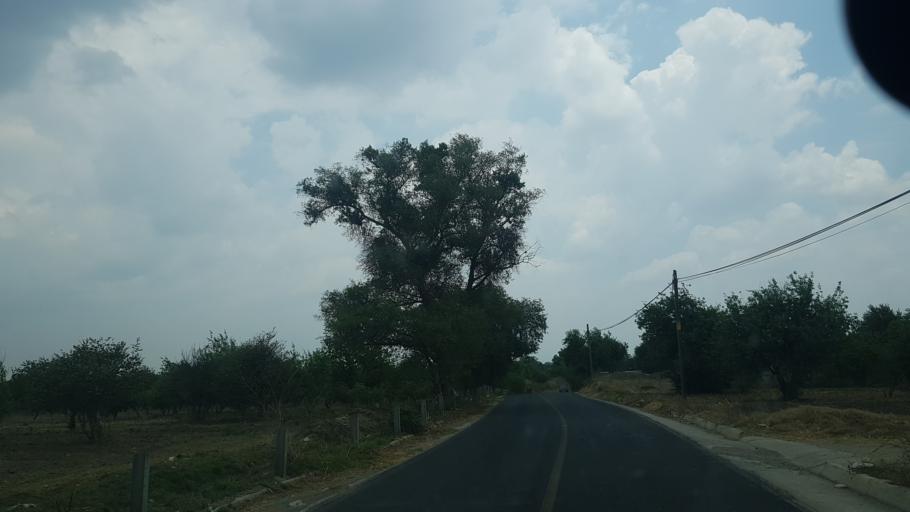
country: MX
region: Puebla
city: Huejotzingo
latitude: 19.1588
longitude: -98.4227
